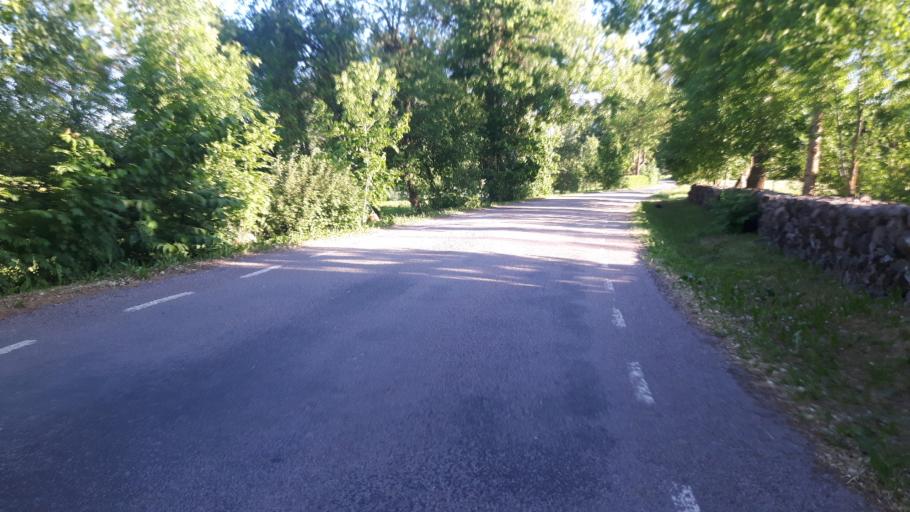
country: EE
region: Raplamaa
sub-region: Kehtna vald
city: Kehtna
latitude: 58.9019
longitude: 24.8792
